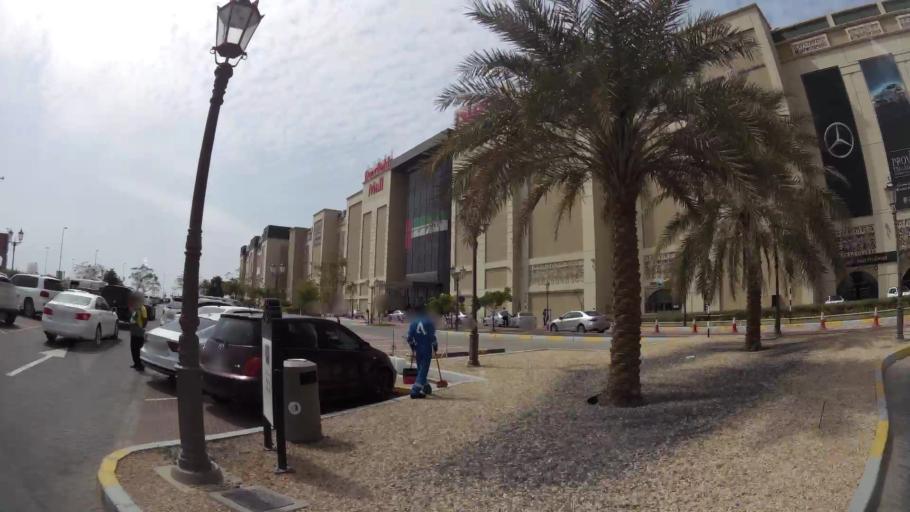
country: AE
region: Abu Dhabi
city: Abu Dhabi
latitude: 24.5236
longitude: 54.6724
